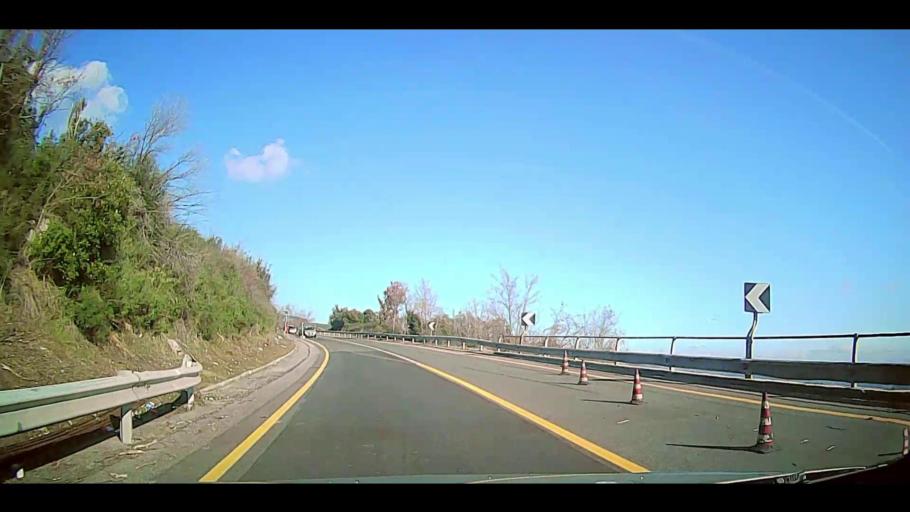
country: IT
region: Calabria
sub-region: Provincia di Crotone
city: Caccuri
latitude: 39.2259
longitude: 16.7958
